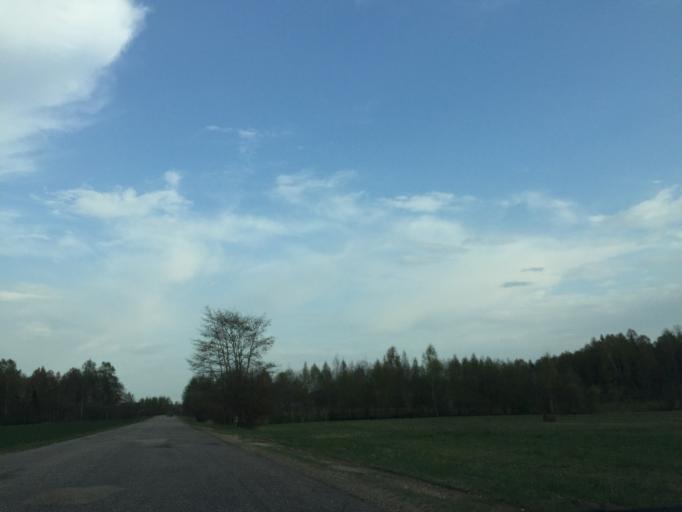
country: LV
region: Malpils
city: Malpils
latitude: 57.0124
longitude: 24.8937
